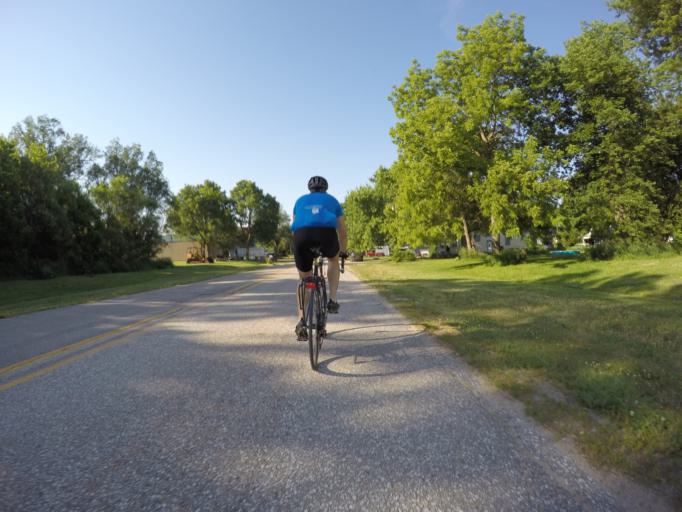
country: US
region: Nebraska
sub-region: Gage County
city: Wymore
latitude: 40.0878
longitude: -96.4828
